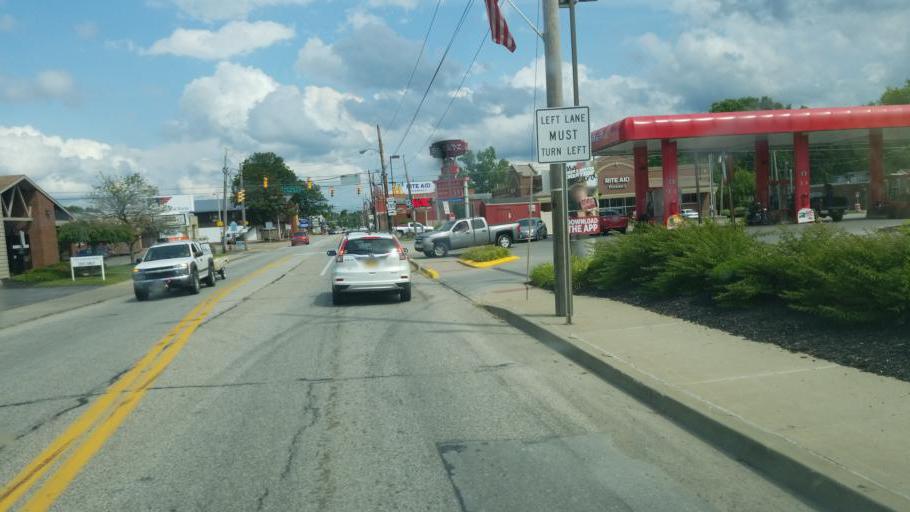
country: US
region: Pennsylvania
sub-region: Crawford County
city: Conneaut Lakeshore
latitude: 41.6033
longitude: -80.3052
